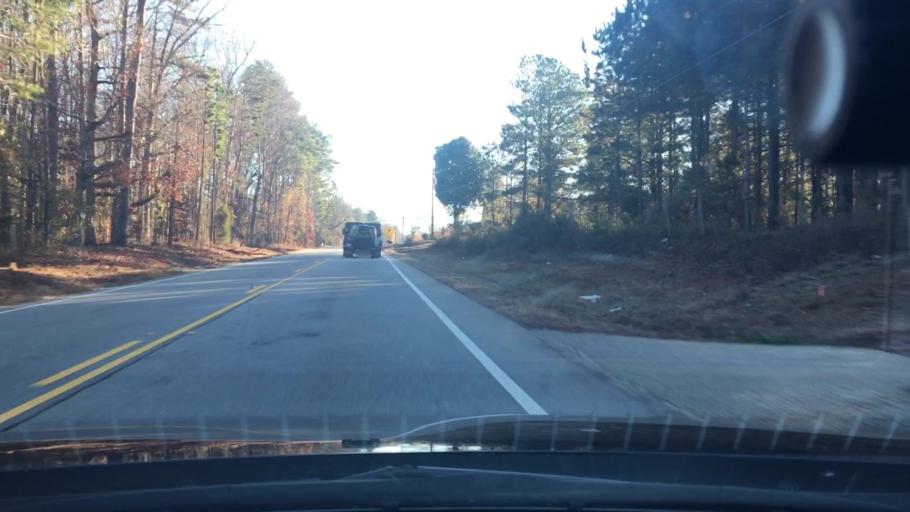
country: US
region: Georgia
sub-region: Spalding County
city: Experiment
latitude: 33.2406
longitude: -84.4162
